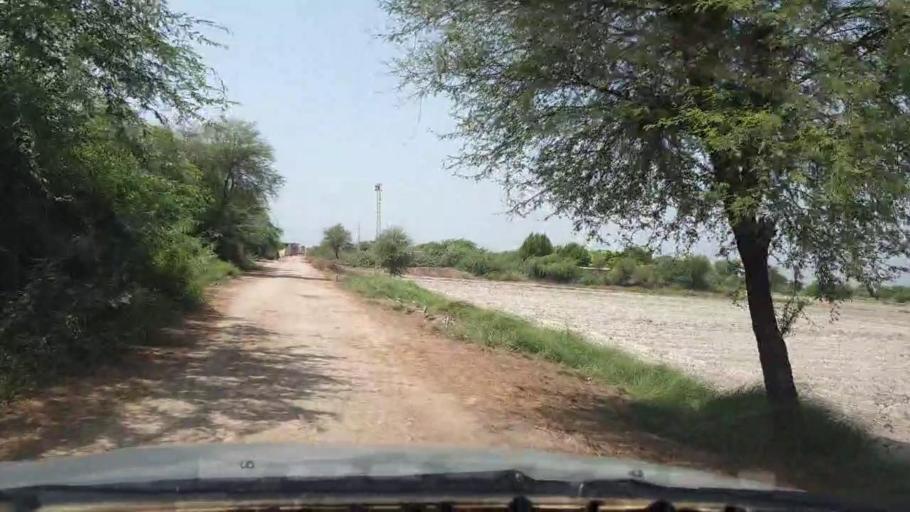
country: PK
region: Sindh
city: Tando Muhammad Khan
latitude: 25.1564
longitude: 68.6316
